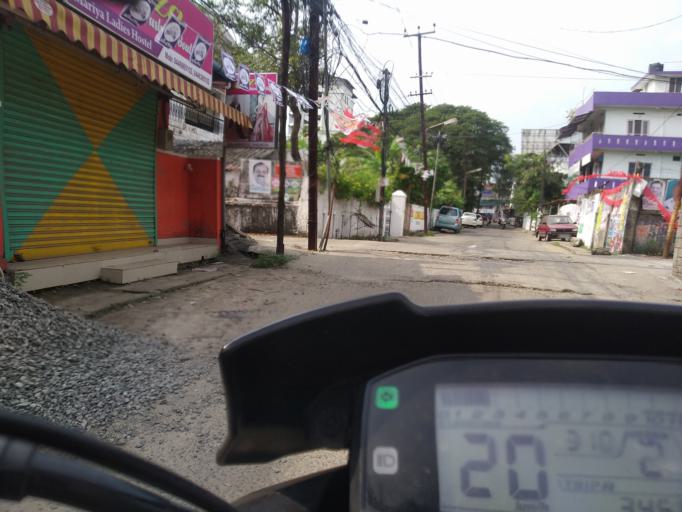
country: IN
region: Kerala
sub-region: Ernakulam
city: Cochin
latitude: 9.9631
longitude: 76.2918
